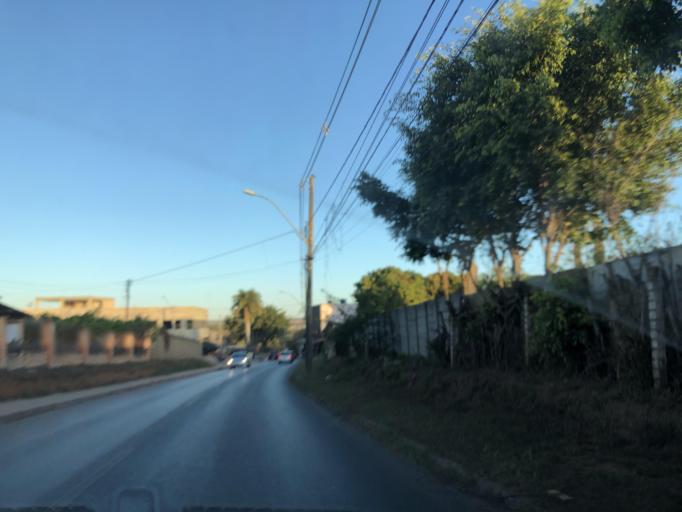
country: BR
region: Federal District
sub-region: Brasilia
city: Brasilia
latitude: -15.8784
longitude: -47.7796
